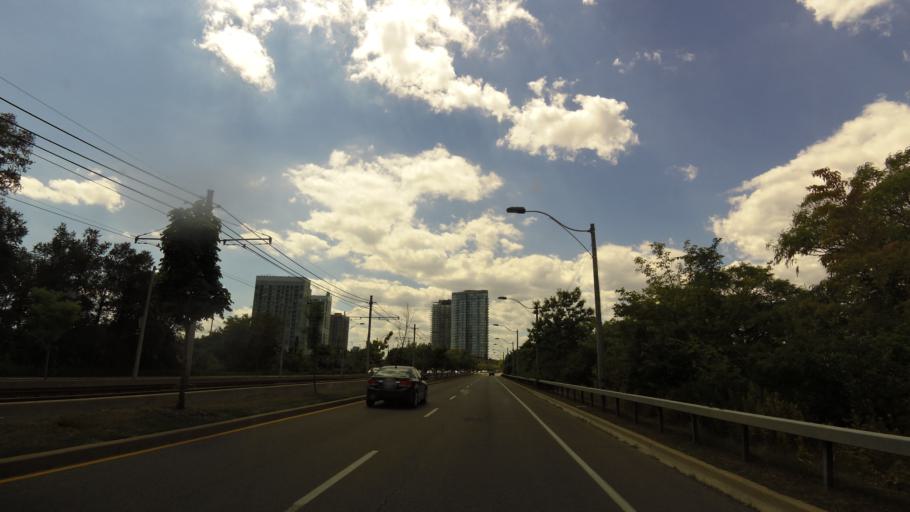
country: CA
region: Ontario
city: Toronto
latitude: 43.6390
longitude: -79.4630
